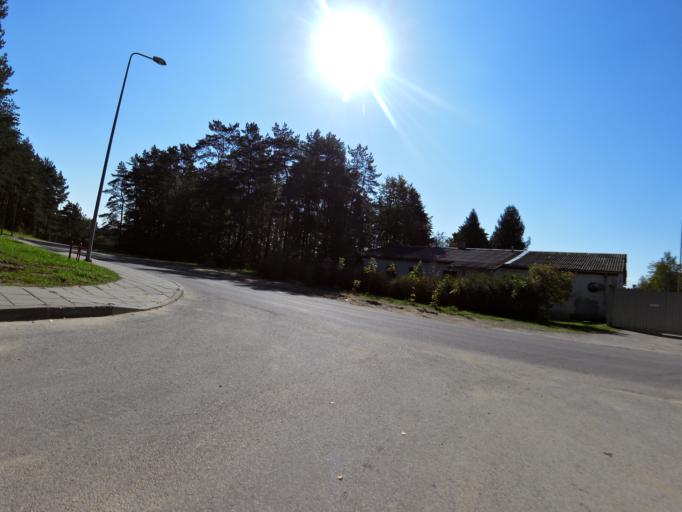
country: LT
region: Vilnius County
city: Lazdynai
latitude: 54.6774
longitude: 25.1916
